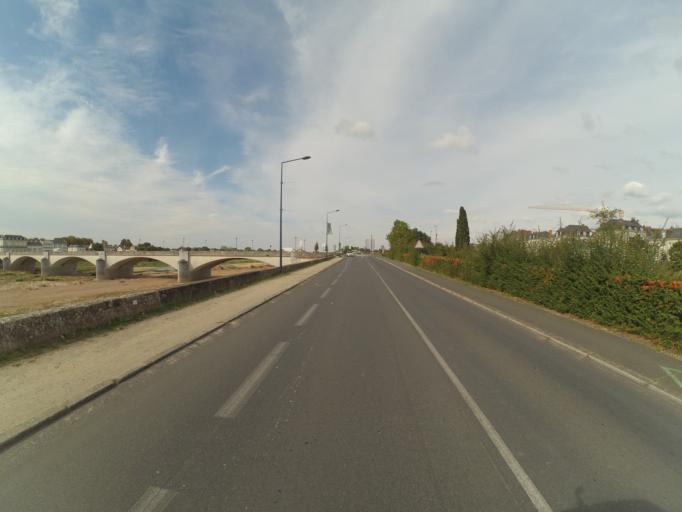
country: FR
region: Pays de la Loire
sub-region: Departement de Maine-et-Loire
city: Saumur
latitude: 47.2667
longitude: -0.0689
